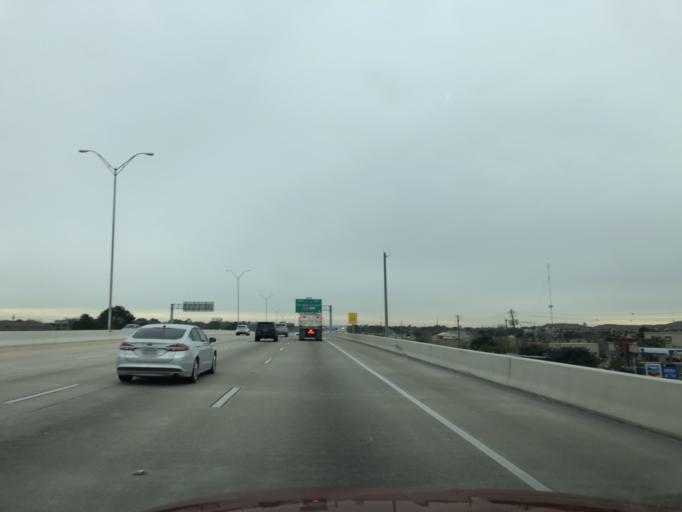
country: US
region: Texas
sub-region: Fort Bend County
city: Missouri City
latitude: 29.6207
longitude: -95.5087
